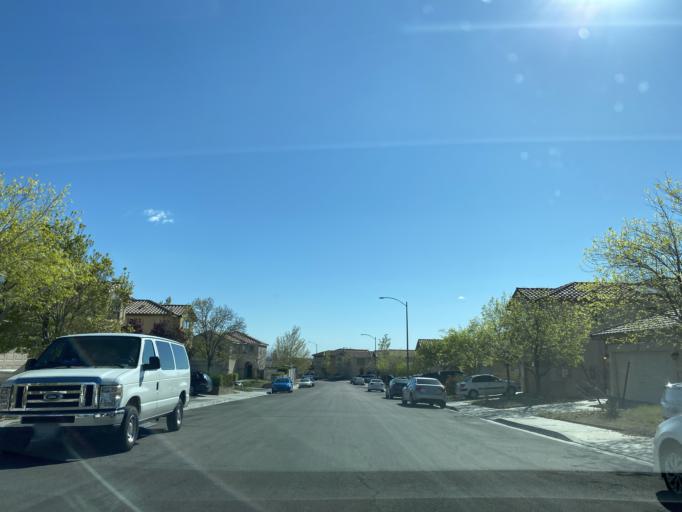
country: US
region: Nevada
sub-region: Clark County
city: Summerlin South
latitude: 36.3031
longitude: -115.2873
